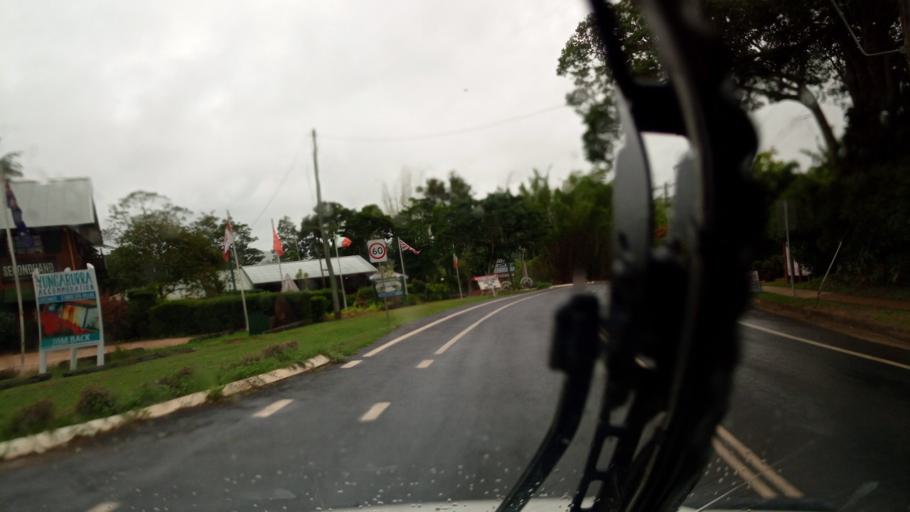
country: AU
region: Queensland
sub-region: Tablelands
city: Tolga
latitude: -17.2734
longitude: 145.5822
